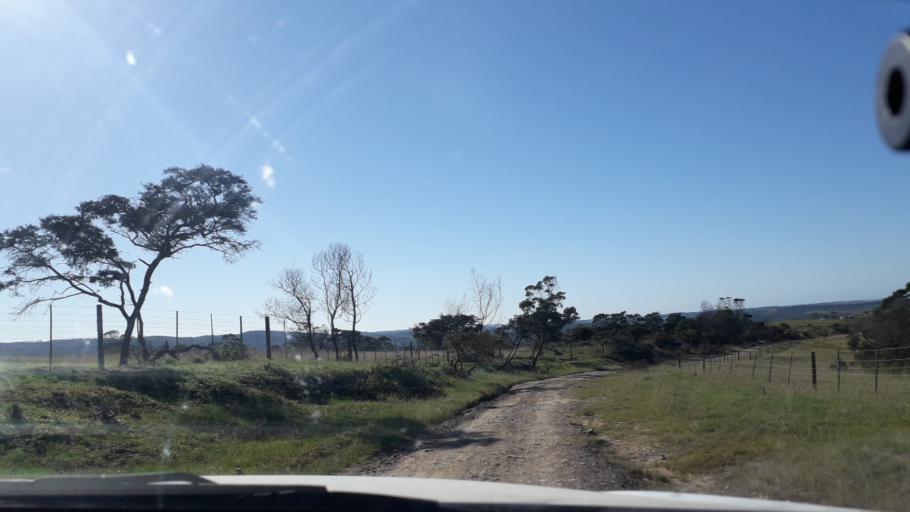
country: ZA
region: Eastern Cape
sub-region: Buffalo City Metropolitan Municipality
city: East London
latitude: -32.8411
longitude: 27.9775
